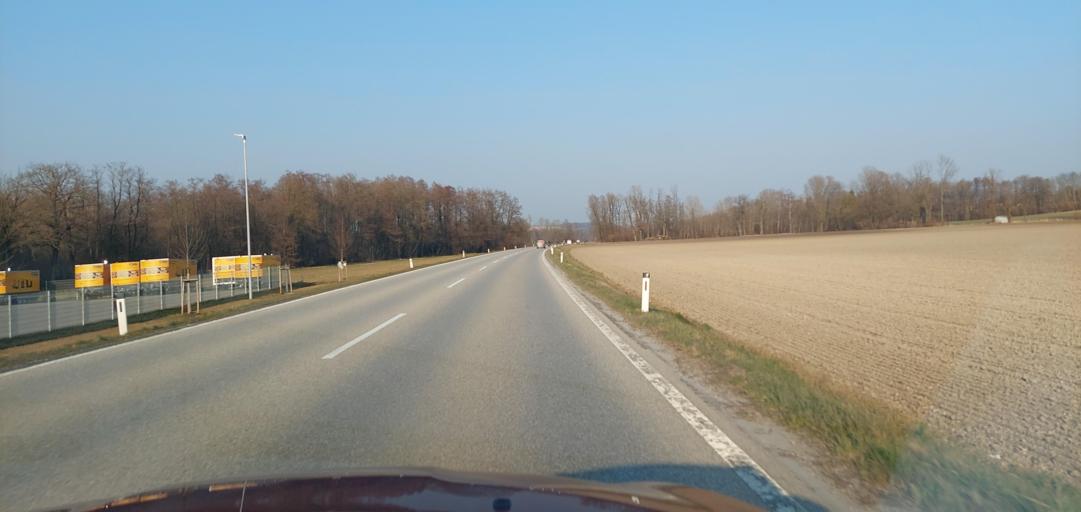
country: AT
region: Upper Austria
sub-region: Politischer Bezirk Grieskirchen
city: Grieskirchen
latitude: 48.2282
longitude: 13.7435
